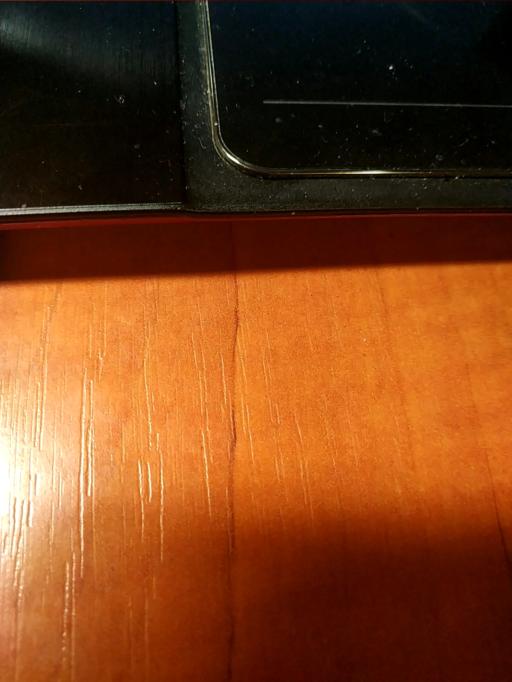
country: RU
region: Tverskaya
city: Likhoslavl'
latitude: 57.1700
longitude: 35.5050
